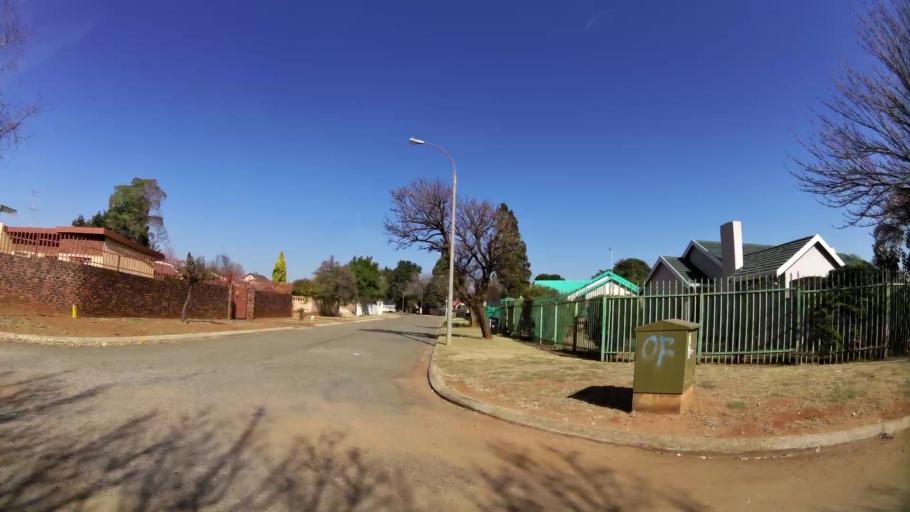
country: ZA
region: Gauteng
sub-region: Ekurhuleni Metropolitan Municipality
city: Tembisa
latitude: -26.0450
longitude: 28.2070
